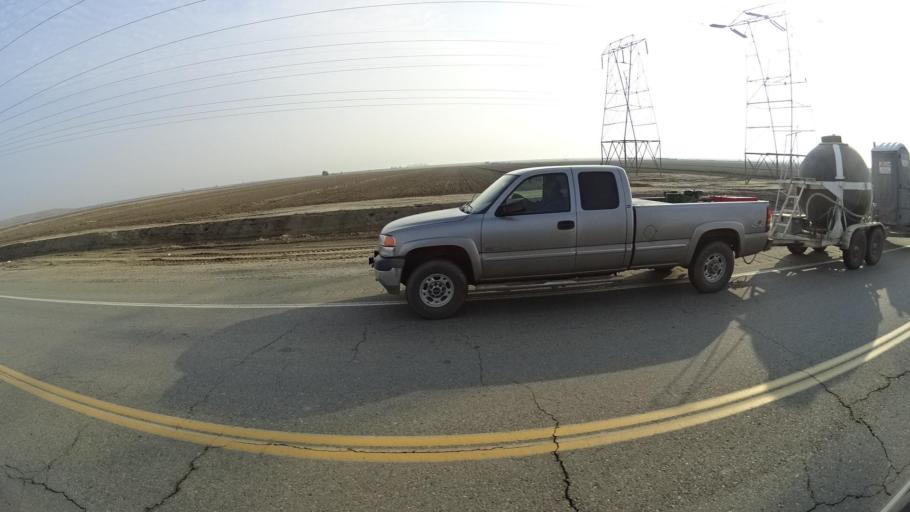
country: US
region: California
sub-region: Kern County
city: Weedpatch
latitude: 35.1783
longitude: -118.9146
